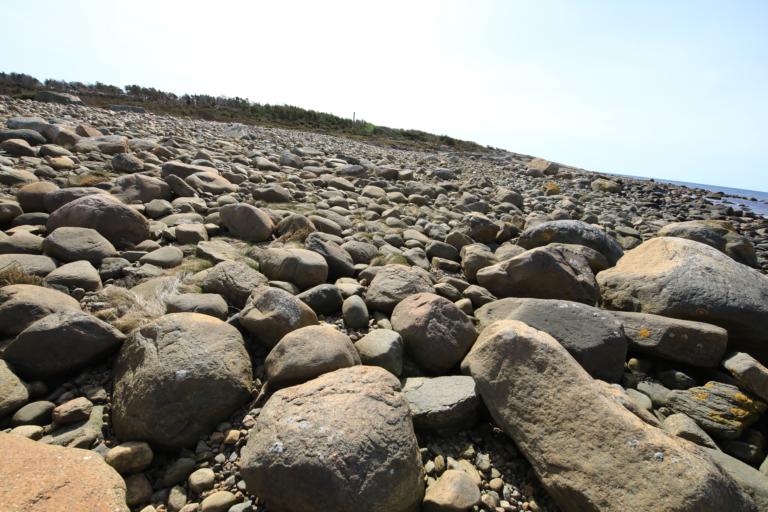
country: SE
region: Halland
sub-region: Kungsbacka Kommun
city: Frillesas
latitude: 57.2738
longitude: 12.1144
